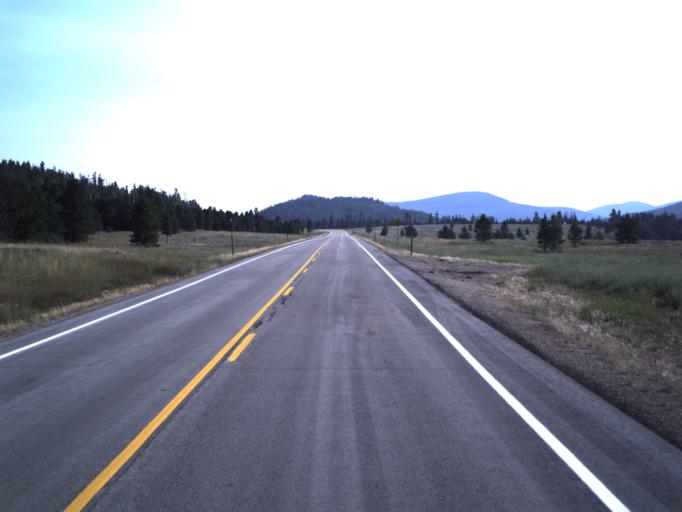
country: US
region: Utah
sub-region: Daggett County
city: Manila
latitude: 40.7914
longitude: -109.4692
